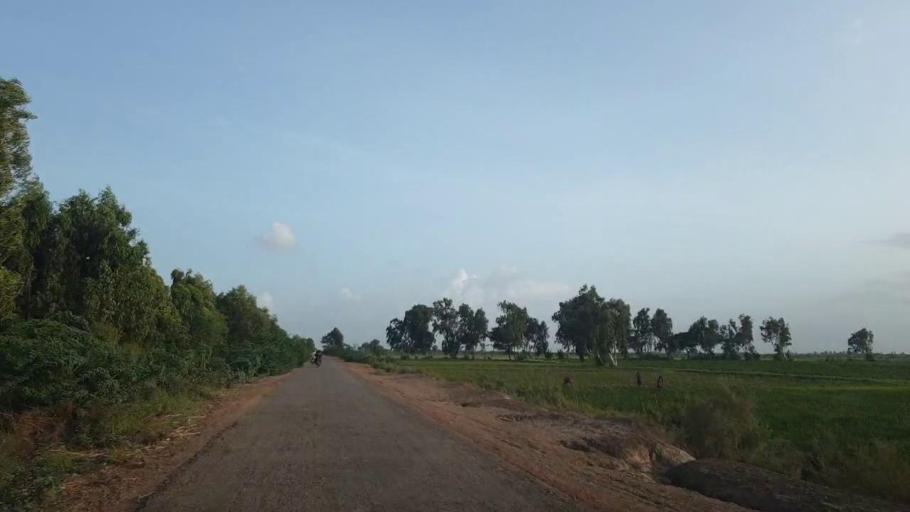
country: PK
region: Sindh
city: Kadhan
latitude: 24.6151
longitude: 69.1158
